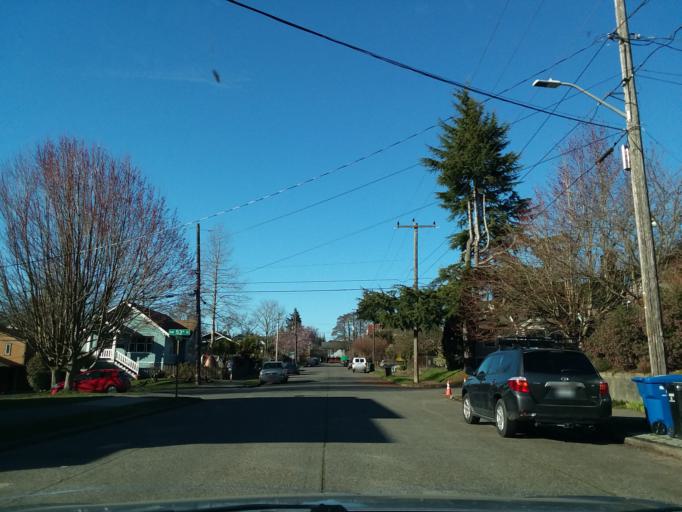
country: US
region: Washington
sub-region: King County
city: Seattle
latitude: 47.6669
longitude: -122.3633
